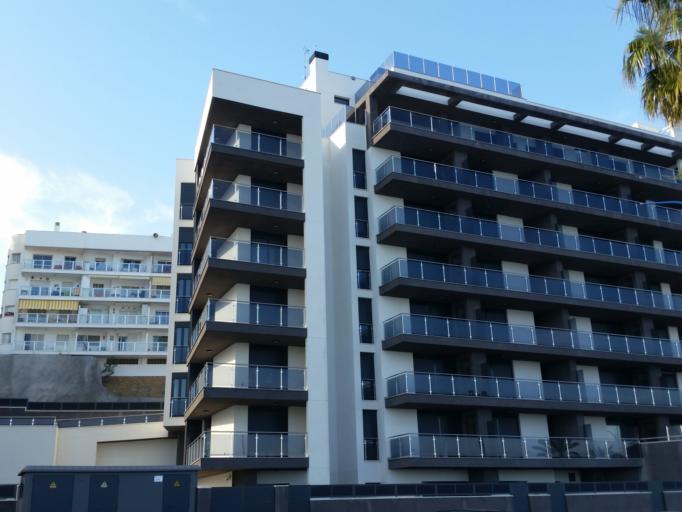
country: ES
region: Andalusia
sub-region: Provincia de Malaga
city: Benalmadena
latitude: 36.5693
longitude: -4.5934
